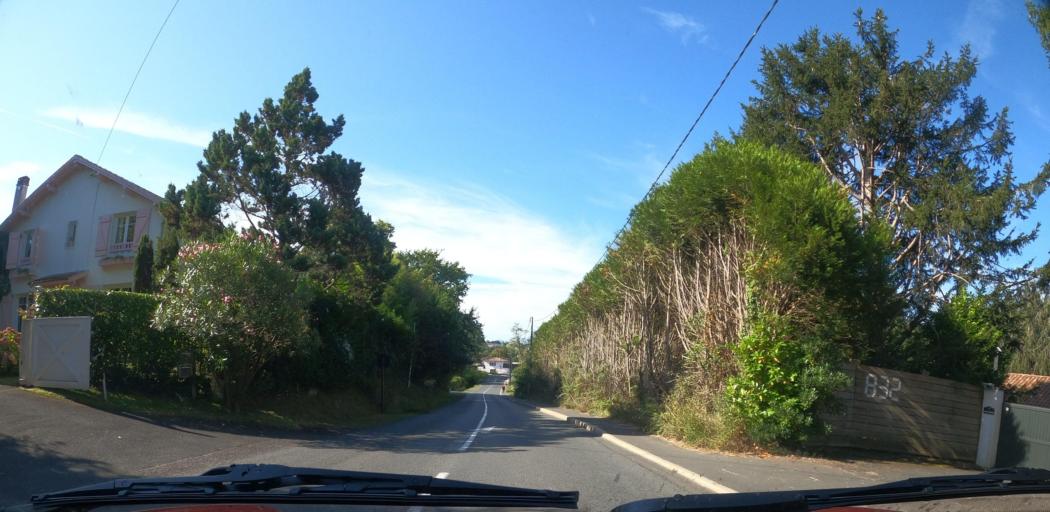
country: FR
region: Aquitaine
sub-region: Departement des Pyrenees-Atlantiques
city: Arbonne
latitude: 43.4412
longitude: -1.5465
